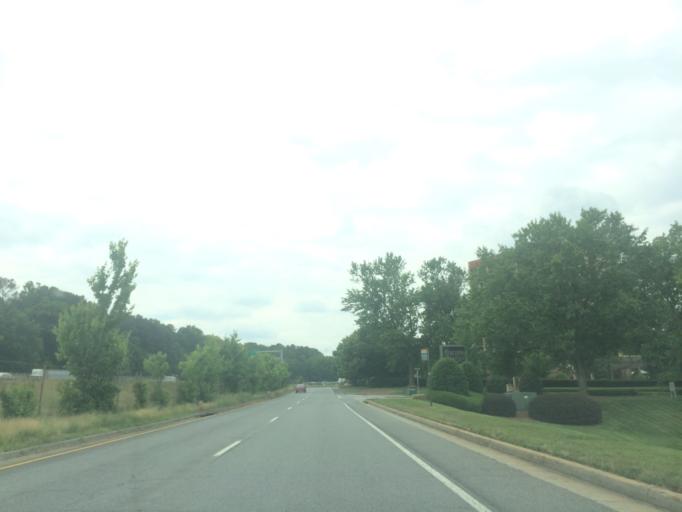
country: US
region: Georgia
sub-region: DeKalb County
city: North Druid Hills
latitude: 33.8456
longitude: -84.3061
